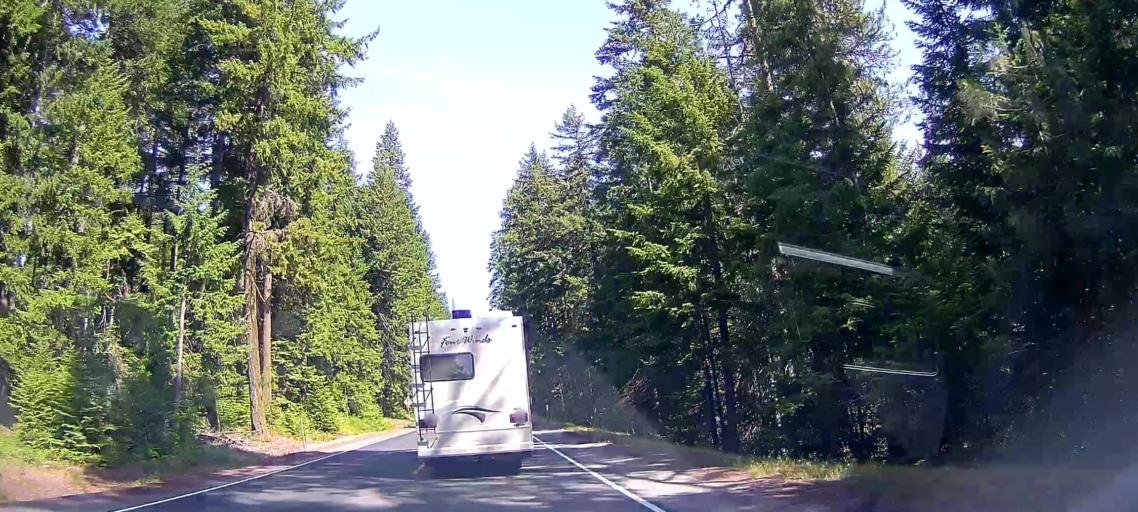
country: US
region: Oregon
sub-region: Jefferson County
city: Warm Springs
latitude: 45.0809
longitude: -121.5411
